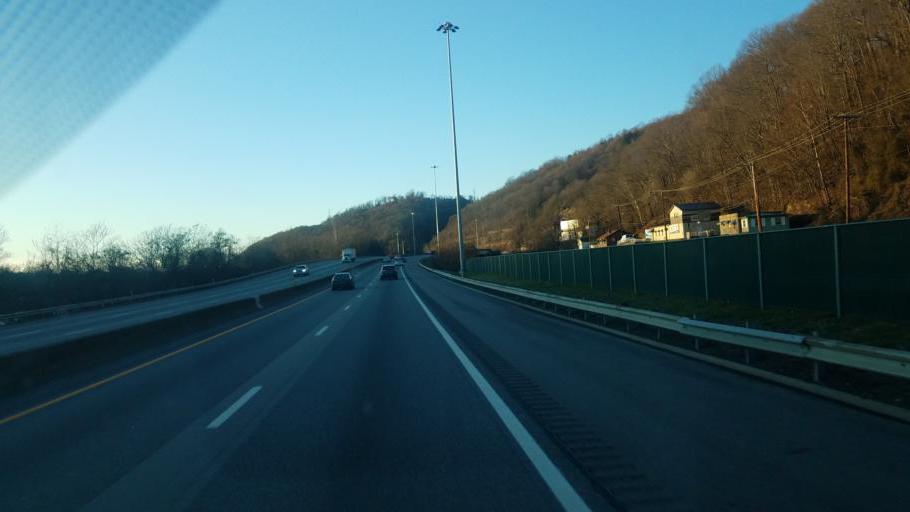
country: US
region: West Virginia
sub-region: Kanawha County
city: Rand
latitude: 38.3274
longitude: -81.5768
